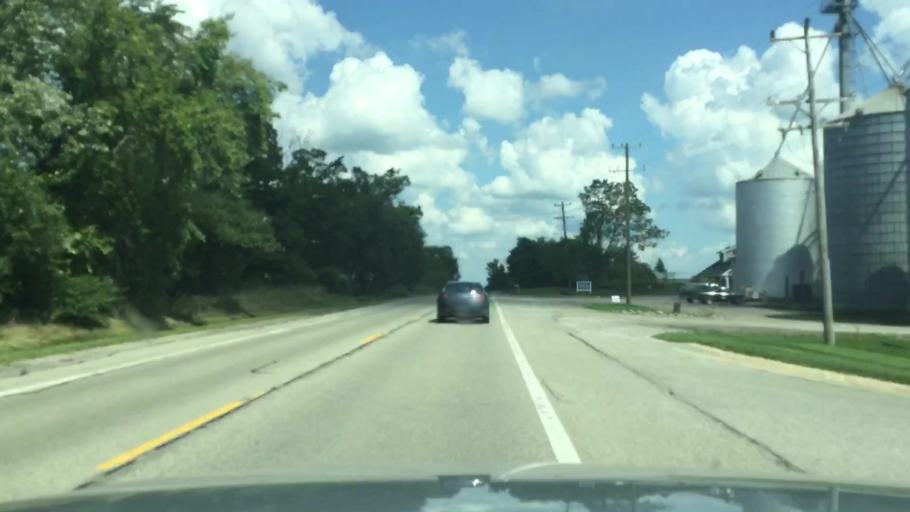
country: US
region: Michigan
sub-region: Washtenaw County
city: Saline
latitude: 42.1488
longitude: -83.8243
